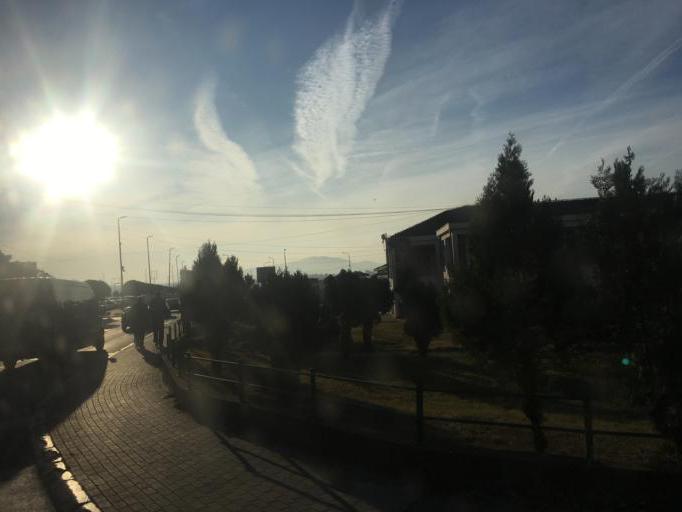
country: XK
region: Pristina
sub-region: Komuna e Drenasit
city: Glogovac
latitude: 42.6219
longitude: 20.8917
